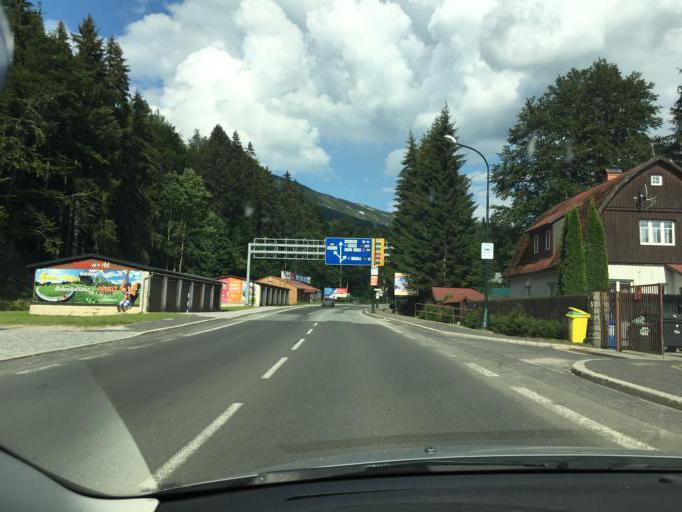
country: CZ
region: Kralovehradecky
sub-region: Okres Trutnov
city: Spindleruv Mlyn
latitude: 50.7247
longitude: 15.5980
